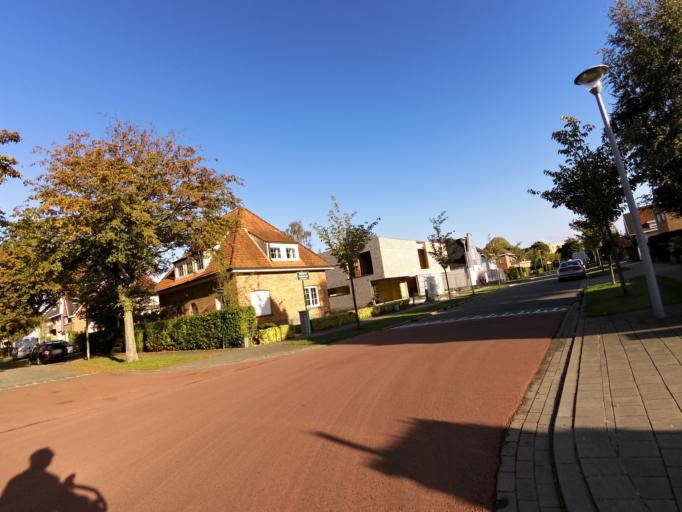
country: BE
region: Flanders
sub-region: Provincie West-Vlaanderen
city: Brugge
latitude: 51.1946
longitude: 3.1925
